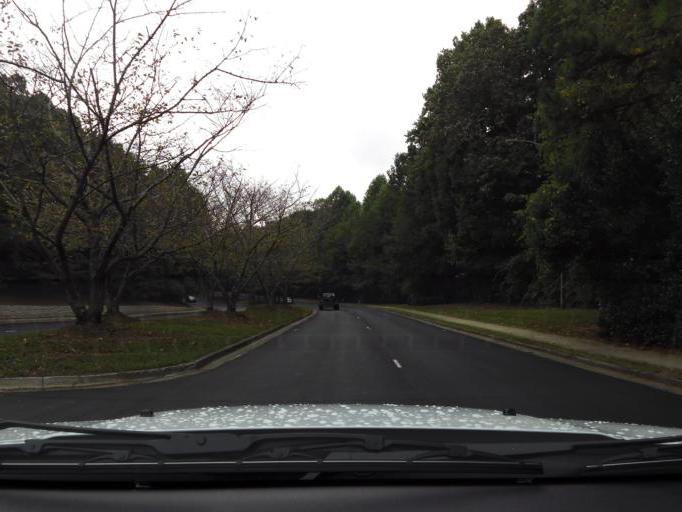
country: US
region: Georgia
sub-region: Cobb County
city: Kennesaw
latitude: 34.0459
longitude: -84.5775
